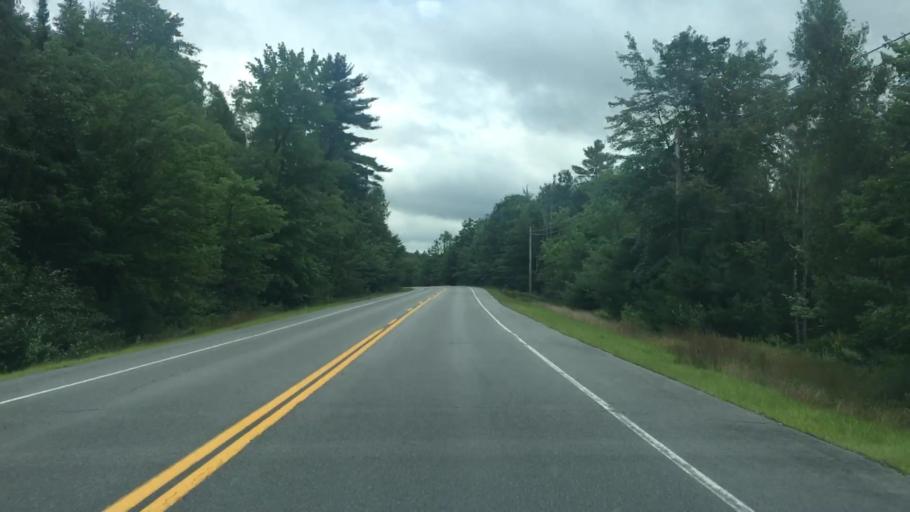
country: US
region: Maine
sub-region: York County
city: Cornish
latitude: 43.7734
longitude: -70.8206
